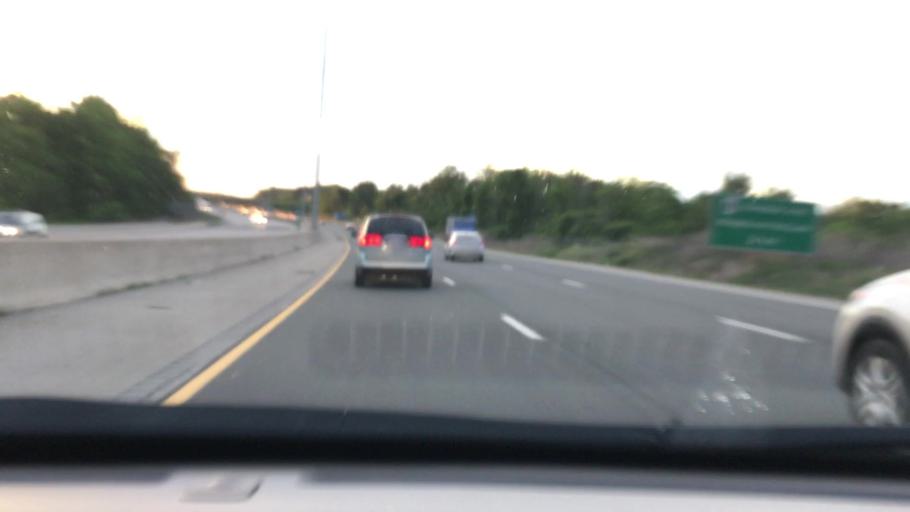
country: CA
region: Ontario
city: Thorold
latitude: 43.1479
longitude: -79.1440
